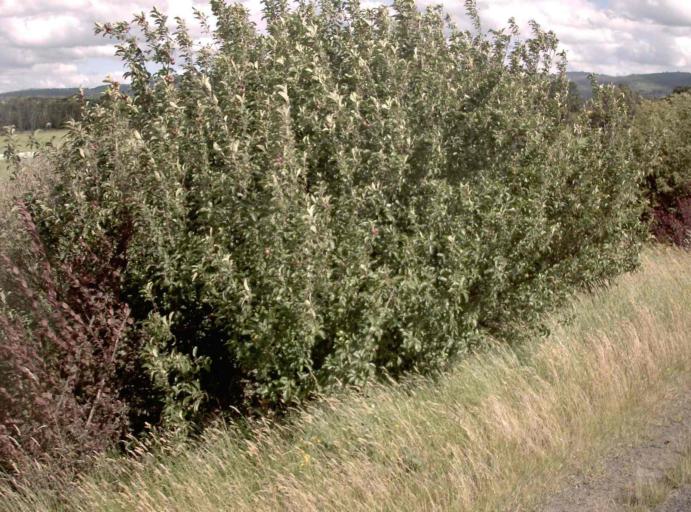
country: AU
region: Victoria
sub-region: Latrobe
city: Morwell
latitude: -38.2873
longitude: 146.4303
